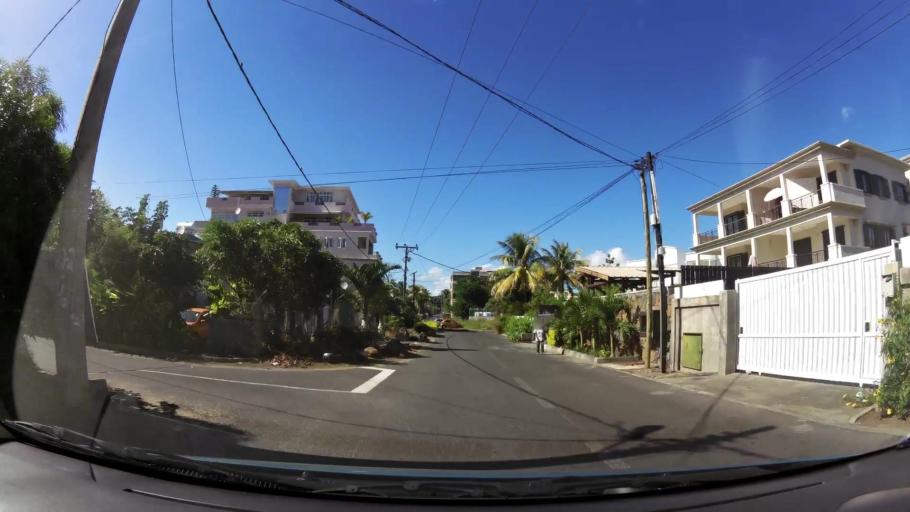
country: MU
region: Black River
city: Flic en Flac
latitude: -20.2809
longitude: 57.3690
